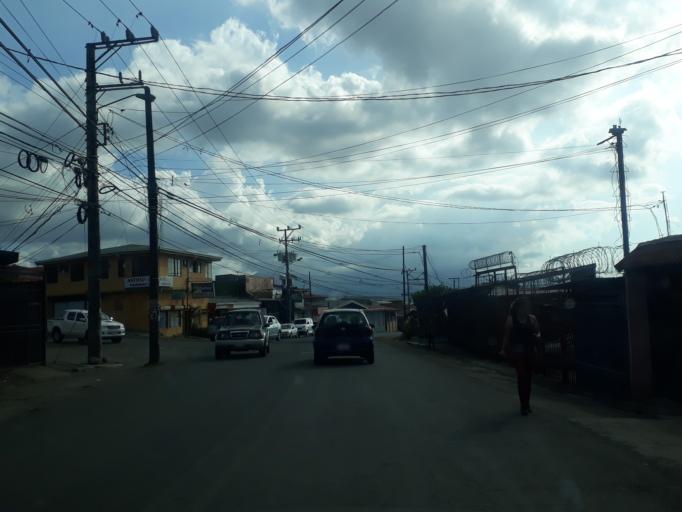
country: CR
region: San Jose
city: Ipis
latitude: 9.9841
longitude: -84.0280
